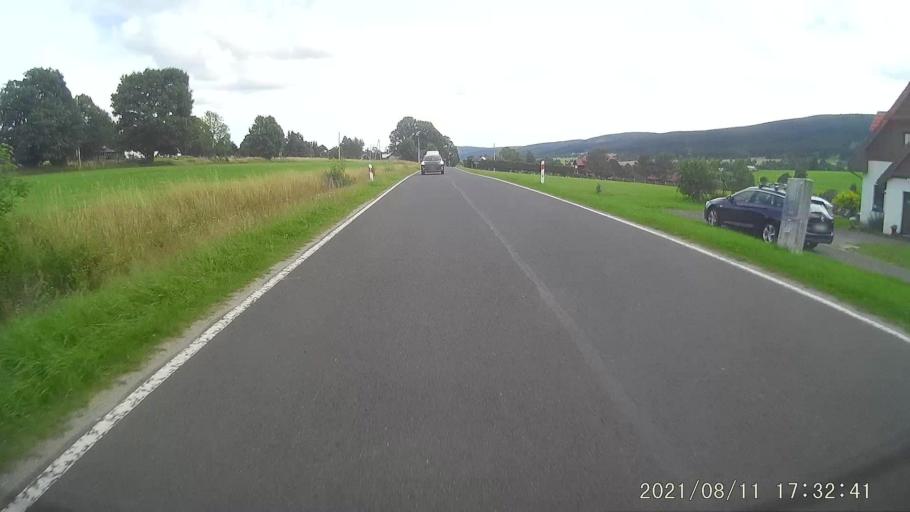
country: PL
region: Lower Silesian Voivodeship
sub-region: Powiat klodzki
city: Szczytna
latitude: 50.3105
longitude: 16.4494
